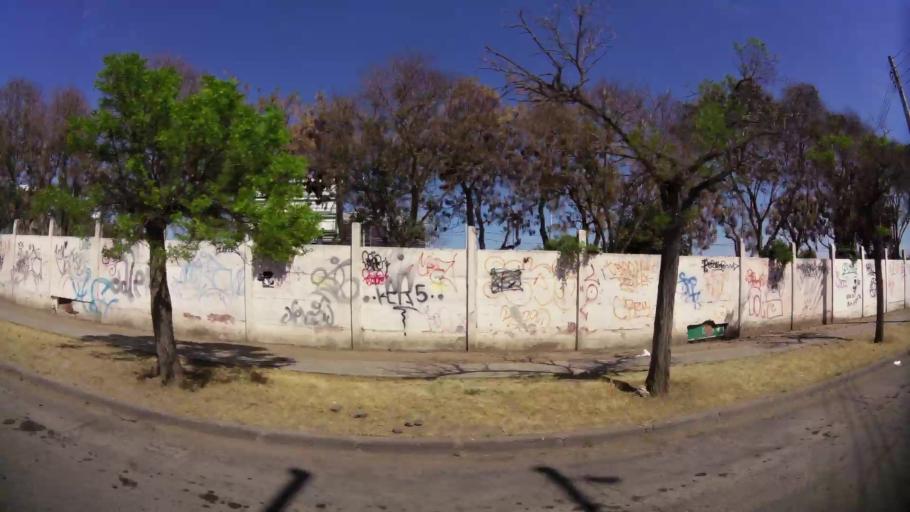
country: CL
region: Santiago Metropolitan
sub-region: Provincia de Santiago
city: Lo Prado
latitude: -33.5065
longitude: -70.7489
